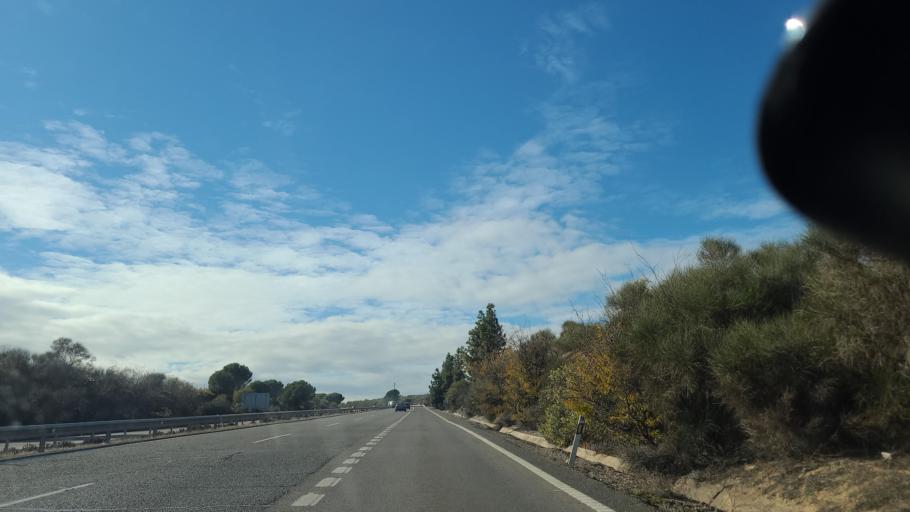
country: ES
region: Andalusia
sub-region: Provincia de Jaen
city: Espeluy
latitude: 38.0710
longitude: -3.8644
